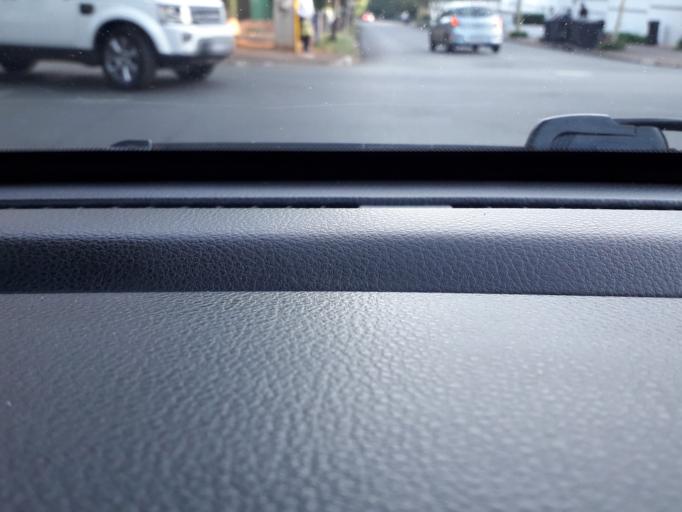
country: ZA
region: Gauteng
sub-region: City of Johannesburg Metropolitan Municipality
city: Johannesburg
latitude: -26.1651
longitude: 28.0497
